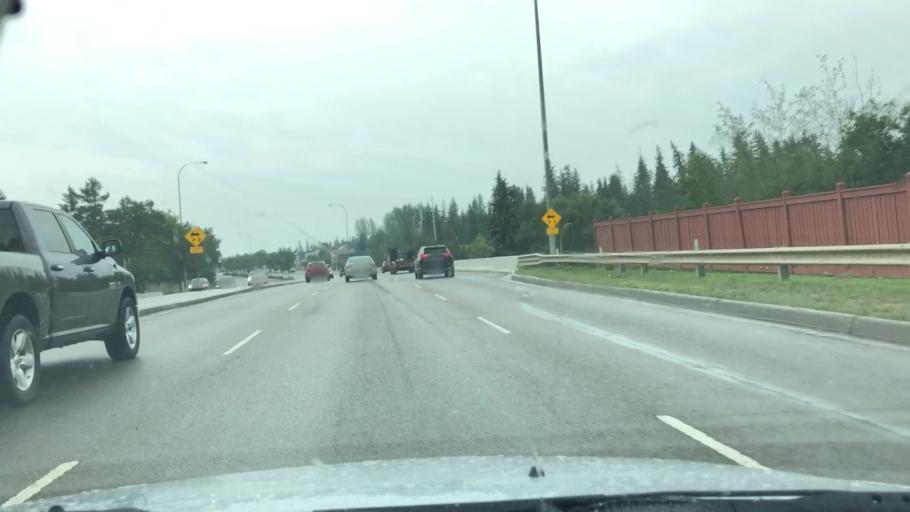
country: CA
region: Alberta
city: St. Albert
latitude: 53.6326
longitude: -113.6227
